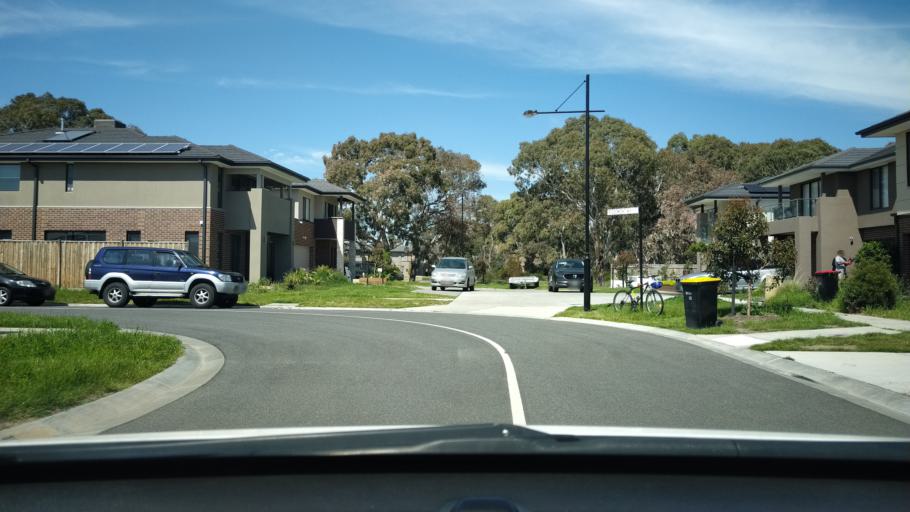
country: AU
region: Victoria
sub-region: Greater Dandenong
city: Keysborough
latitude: -38.0018
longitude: 145.1783
